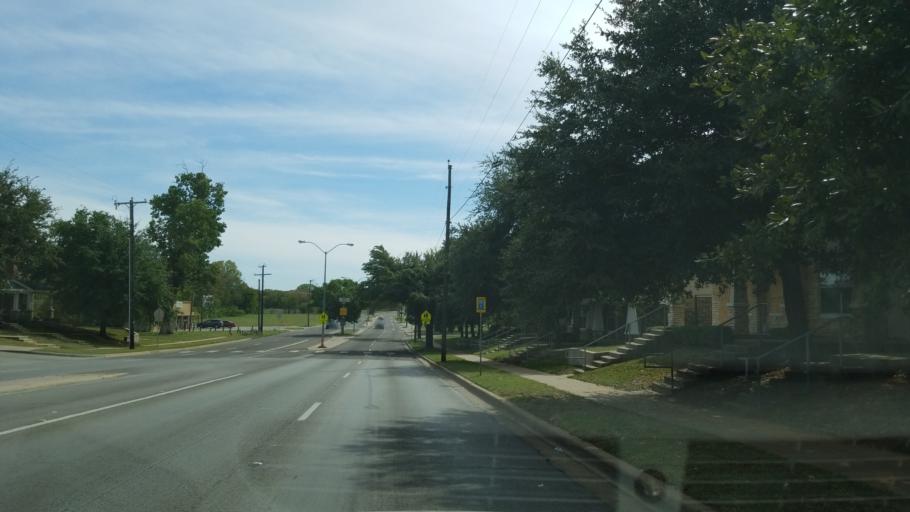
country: US
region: Texas
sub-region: Dallas County
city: Dallas
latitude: 32.7742
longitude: -96.7382
